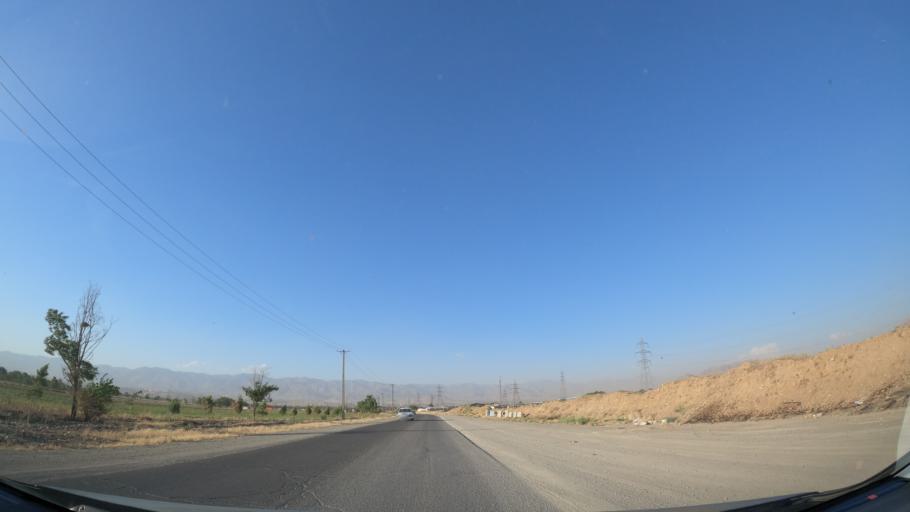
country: IR
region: Alborz
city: Hashtgerd
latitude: 35.9199
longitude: 50.7386
